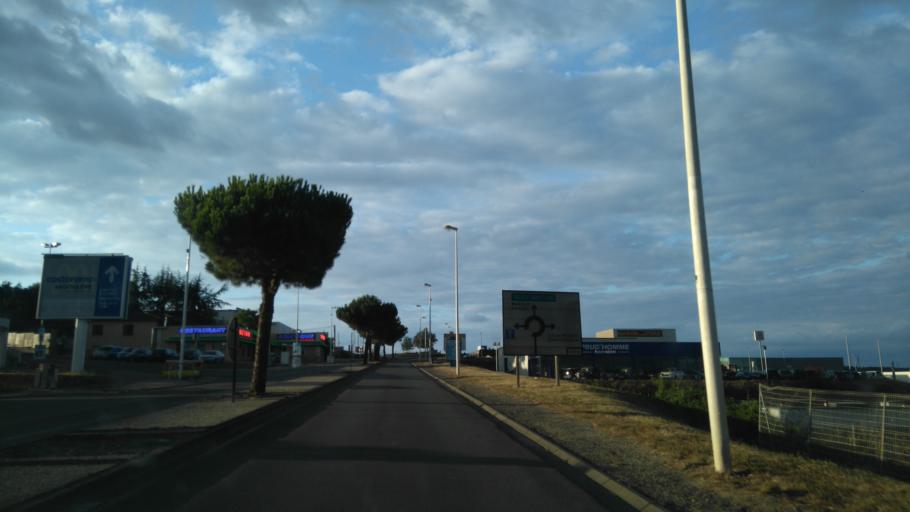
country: FR
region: Poitou-Charentes
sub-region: Departement de la Charente
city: Gond-Pontouvre
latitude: 45.6851
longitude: 0.1783
